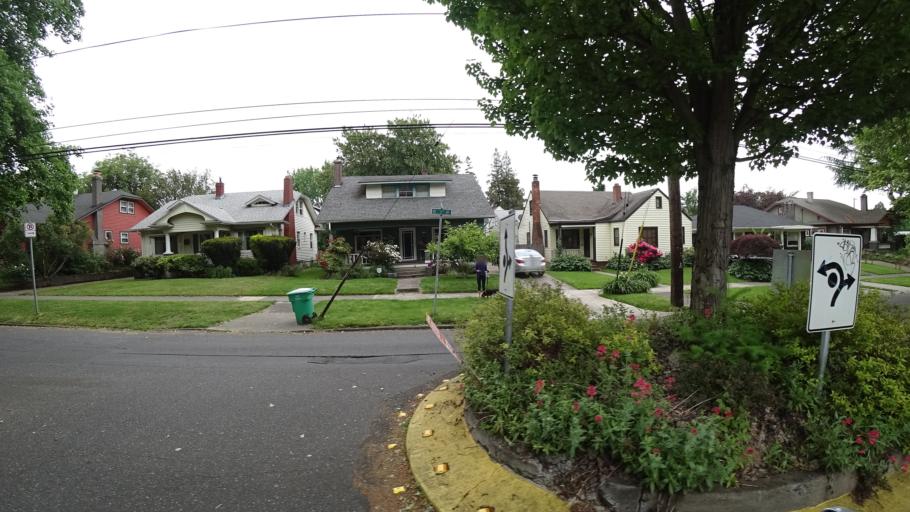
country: US
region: Oregon
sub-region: Multnomah County
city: Portland
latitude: 45.5430
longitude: -122.6587
